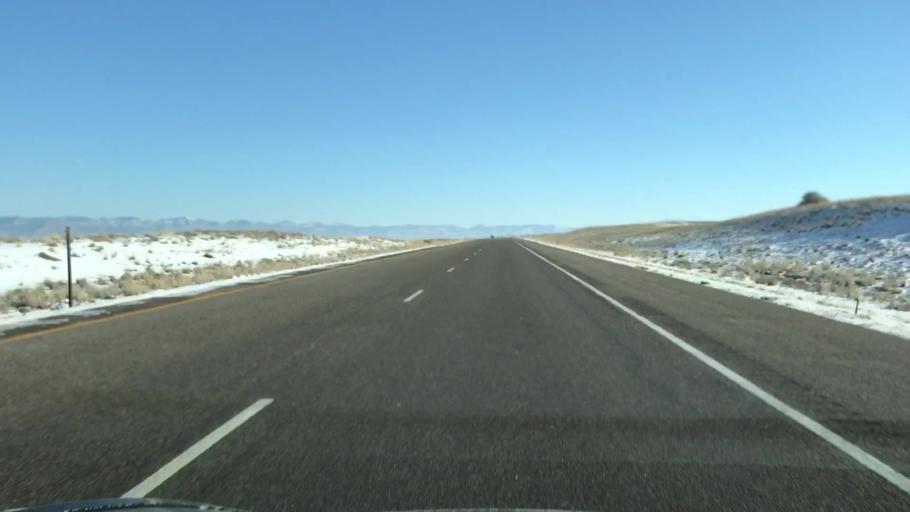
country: US
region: Colorado
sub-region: Mesa County
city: Loma
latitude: 39.2260
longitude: -108.9293
